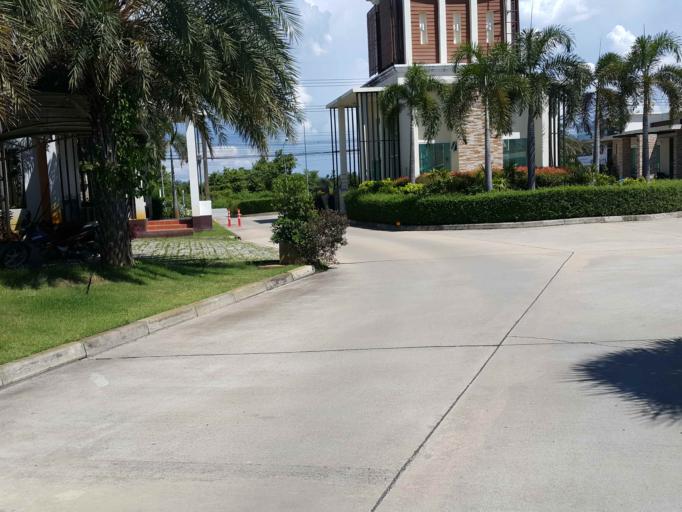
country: TH
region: Chiang Mai
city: San Kamphaeng
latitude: 18.7570
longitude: 99.0747
